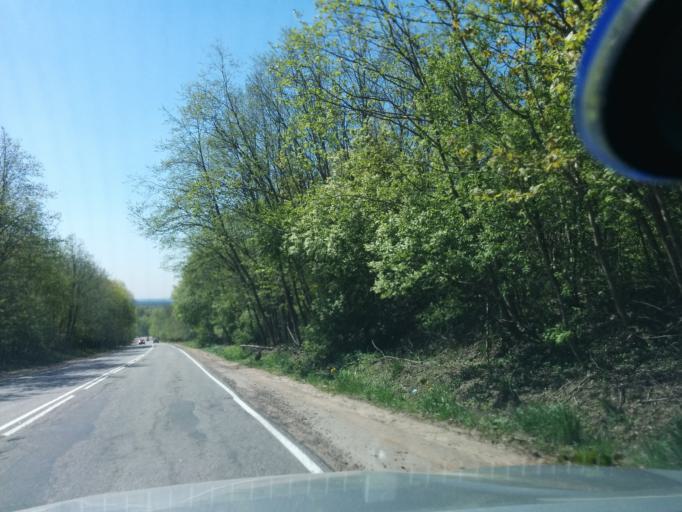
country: RU
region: Leningrad
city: Verkhniye Osel'ki
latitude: 60.2398
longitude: 30.4406
